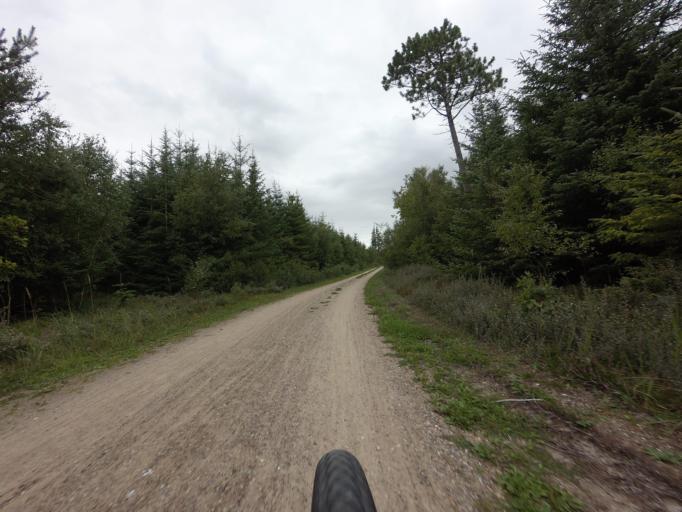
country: DK
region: North Denmark
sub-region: Hjorring Kommune
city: Hirtshals
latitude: 57.5834
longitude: 10.0879
